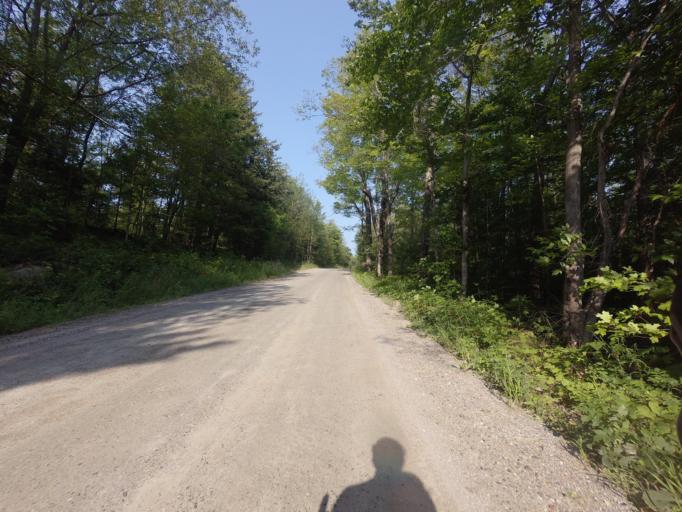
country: CA
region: Ontario
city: Perth
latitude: 44.7998
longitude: -76.7484
